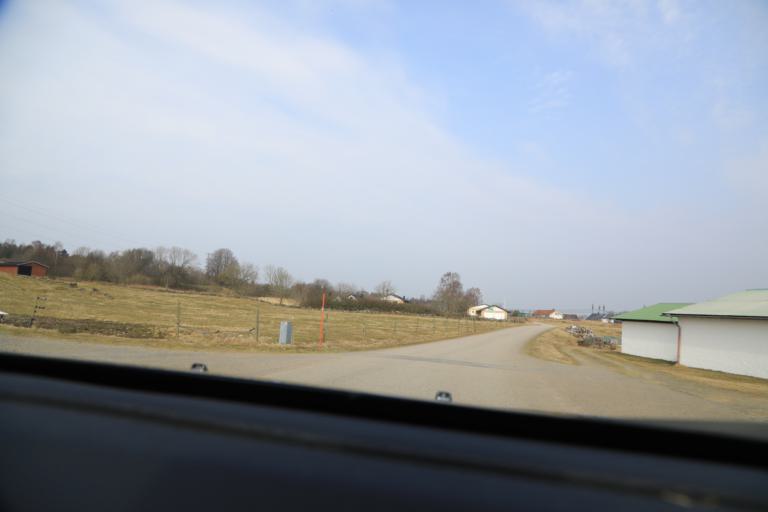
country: SE
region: Halland
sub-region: Kungsbacka Kommun
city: Frillesas
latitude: 57.2683
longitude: 12.1552
